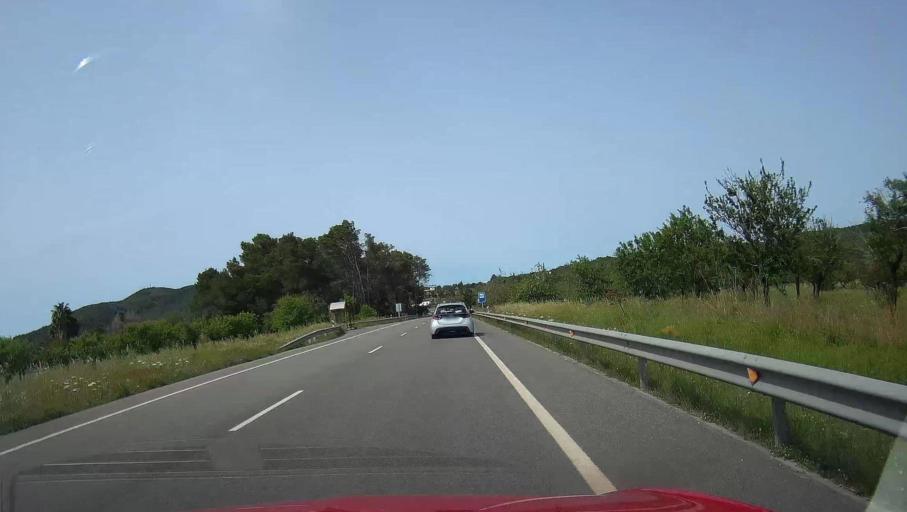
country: ES
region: Balearic Islands
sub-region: Illes Balears
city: Sant Joan de Labritja
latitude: 39.0582
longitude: 1.4941
